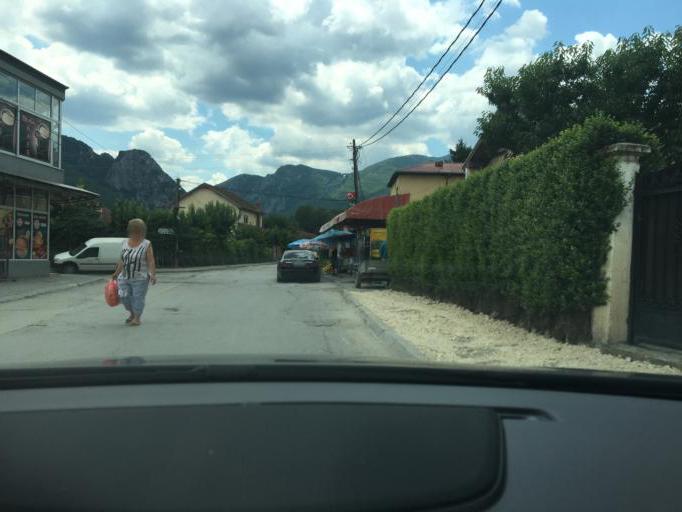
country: MK
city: Ljubin
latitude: 41.9819
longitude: 21.3076
